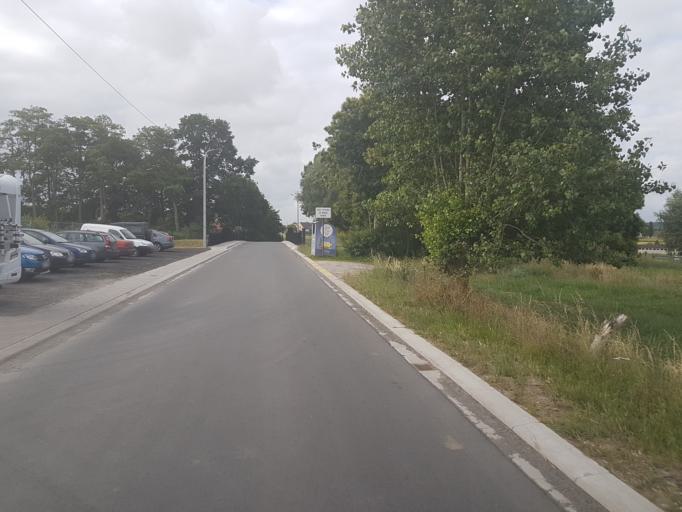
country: BE
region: Flanders
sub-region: Provincie West-Vlaanderen
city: Waregem
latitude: 50.8336
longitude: 3.4153
